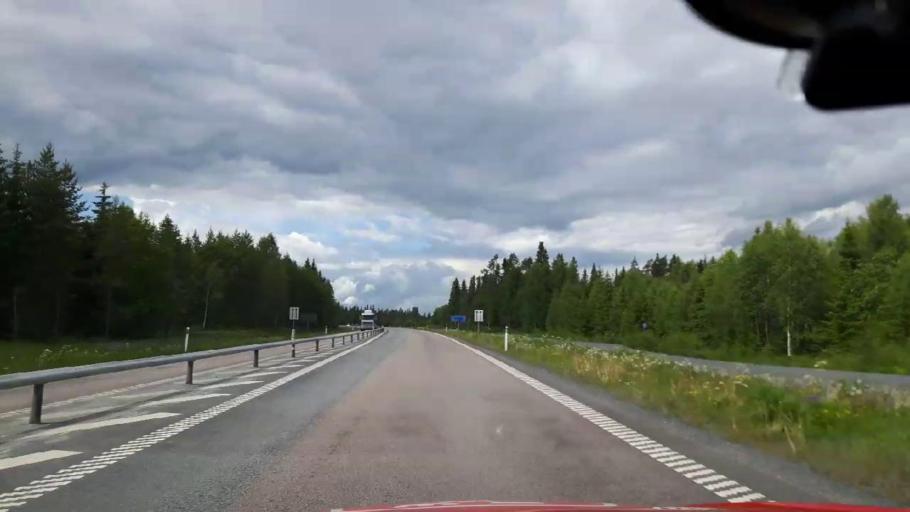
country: SE
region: Jaemtland
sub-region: OEstersunds Kommun
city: Ostersund
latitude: 63.2495
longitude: 14.5885
